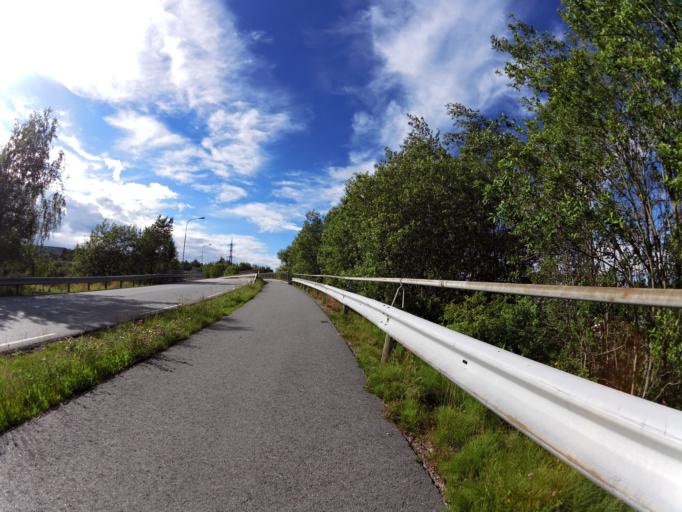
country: NO
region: Ostfold
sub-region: Fredrikstad
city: Fredrikstad
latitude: 59.2585
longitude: 11.0104
